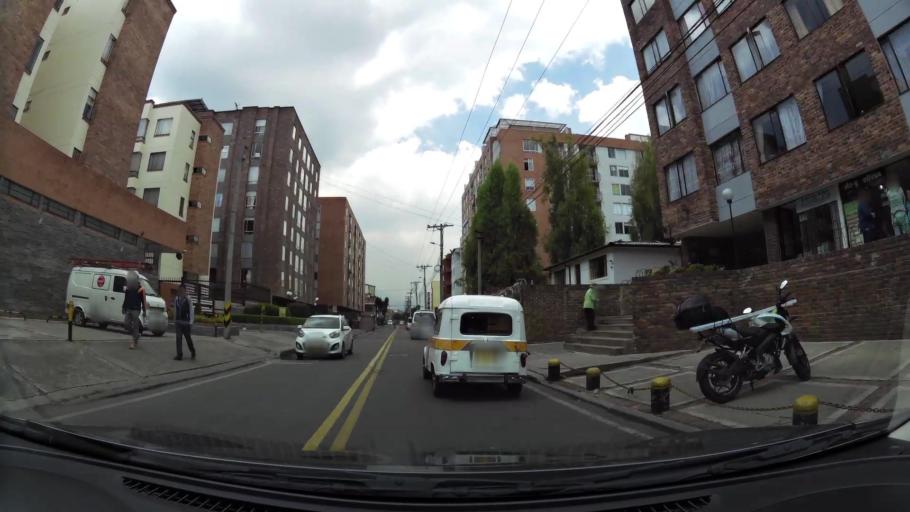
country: CO
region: Cundinamarca
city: La Calera
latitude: 4.7453
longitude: -74.0307
